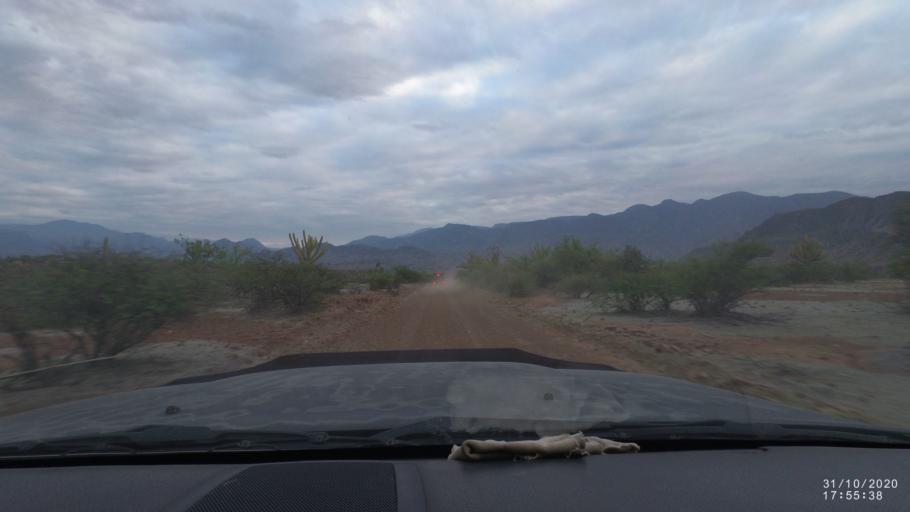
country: BO
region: Chuquisaca
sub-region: Provincia Zudanez
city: Mojocoya
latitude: -18.6454
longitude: -64.5283
